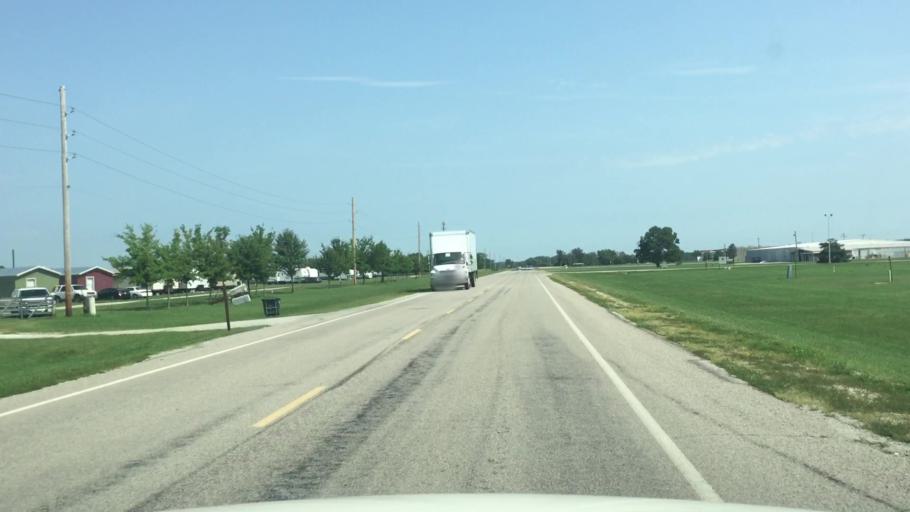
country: US
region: Kansas
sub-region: Montgomery County
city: Coffeyville
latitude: 37.0972
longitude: -95.5861
